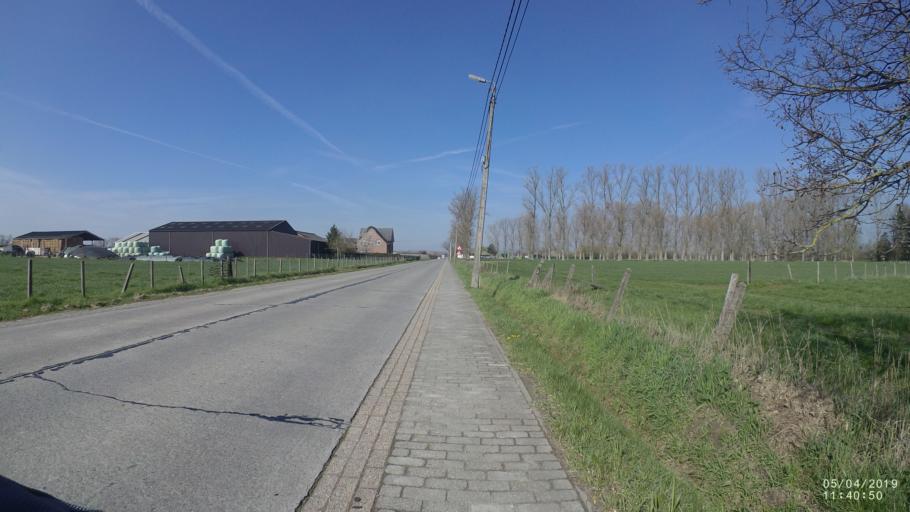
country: BE
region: Flanders
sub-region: Provincie Vlaams-Brabant
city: Geetbets
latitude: 50.8960
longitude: 5.1546
